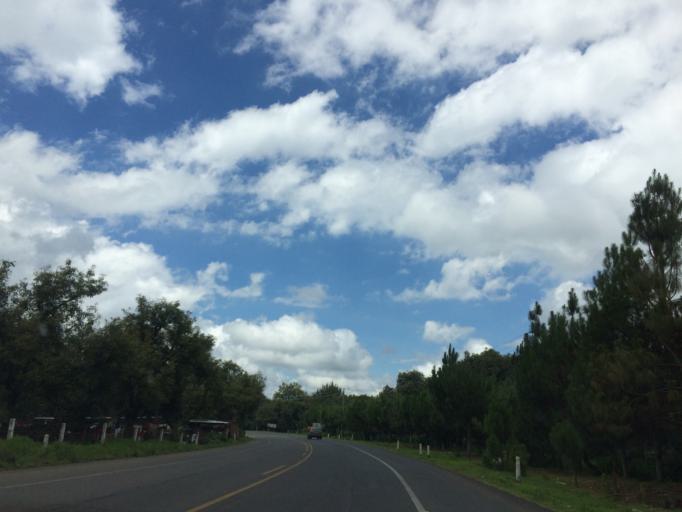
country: MX
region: Michoacan
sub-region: Uruapan
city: Nuevo Zirosto
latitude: 19.5485
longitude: -102.3395
